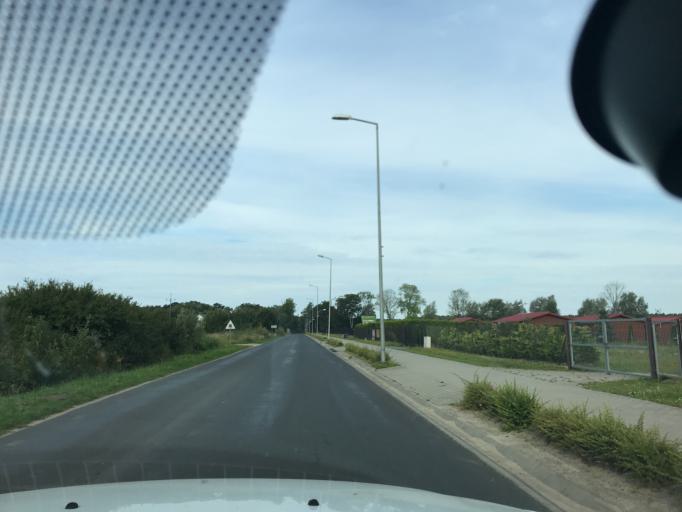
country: PL
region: West Pomeranian Voivodeship
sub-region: Powiat slawienski
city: Slawno
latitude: 54.5339
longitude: 16.5776
